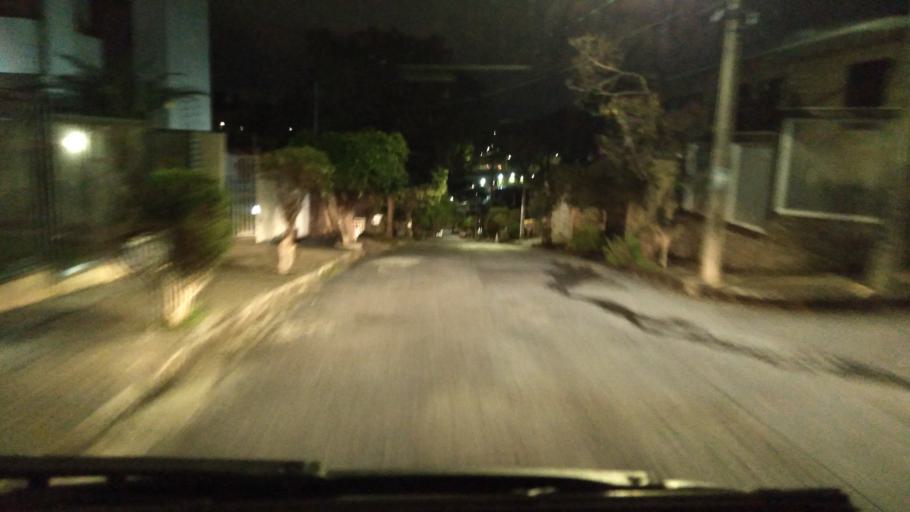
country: BR
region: Minas Gerais
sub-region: Belo Horizonte
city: Belo Horizonte
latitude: -19.8939
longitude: -43.9728
